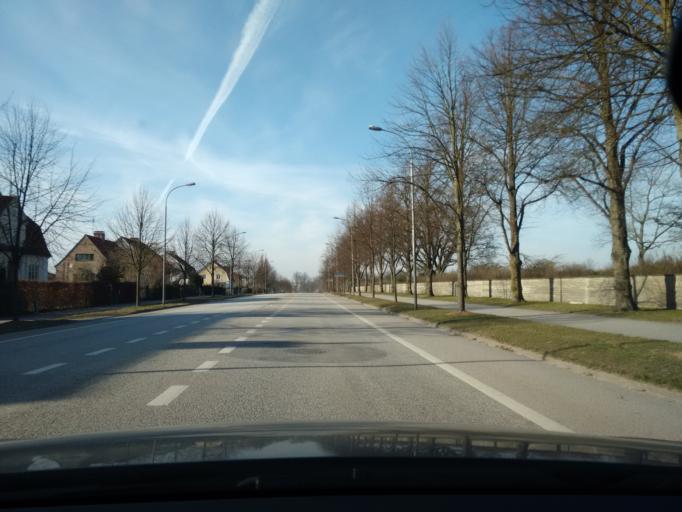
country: SE
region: Skane
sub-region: Lunds Kommun
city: Lund
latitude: 55.7150
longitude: 13.1878
